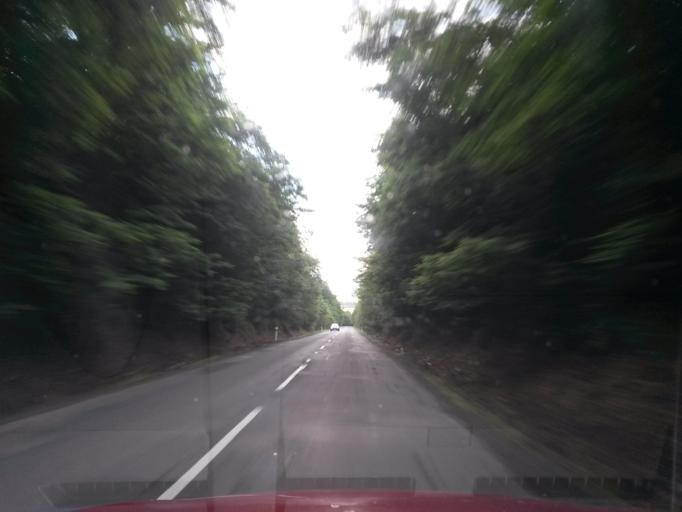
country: SK
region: Banskobystricky
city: Lucenec
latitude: 48.3295
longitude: 19.5389
